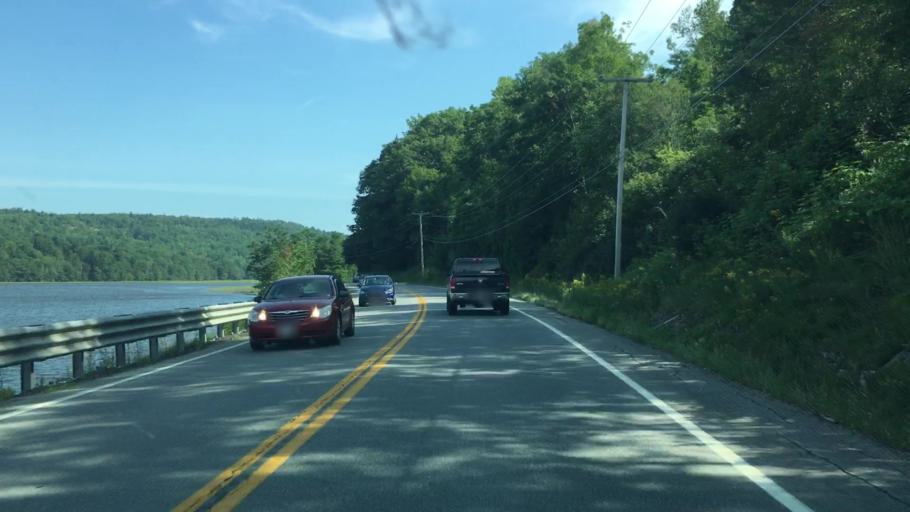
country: US
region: Maine
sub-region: Waldo County
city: Frankfort
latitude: 44.5990
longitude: -68.8672
